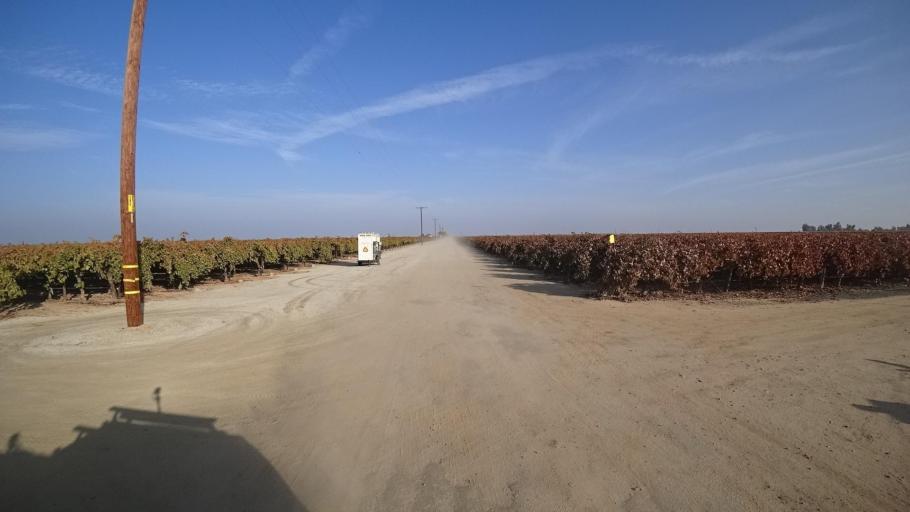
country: US
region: California
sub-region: Kern County
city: Delano
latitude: 35.7397
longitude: -119.1873
